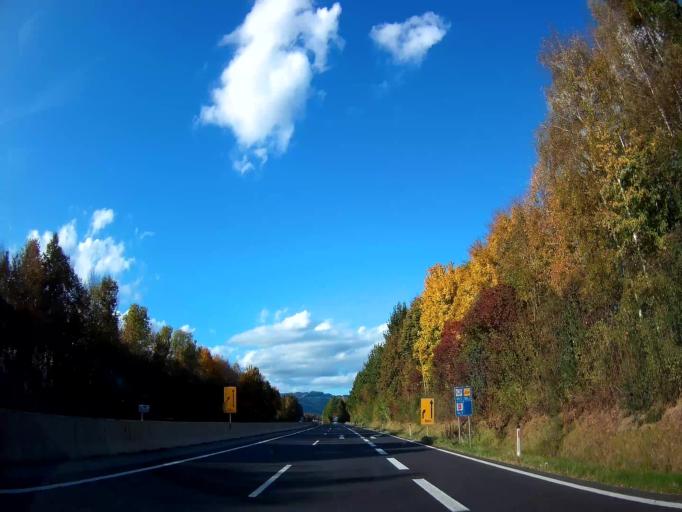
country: AT
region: Carinthia
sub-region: Politischer Bezirk Wolfsberg
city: Wolfsberg
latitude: 46.8189
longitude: 14.8222
